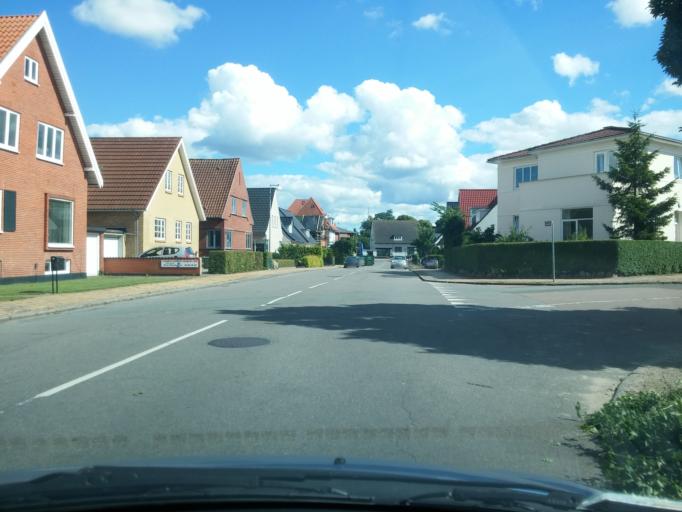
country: DK
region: South Denmark
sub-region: Odense Kommune
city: Odense
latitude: 55.4098
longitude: 10.4038
